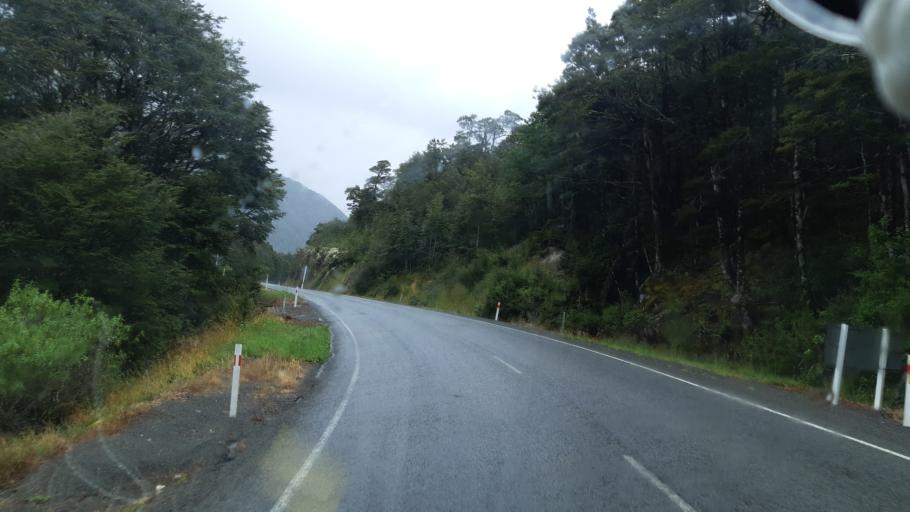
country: NZ
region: Canterbury
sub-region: Hurunui District
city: Amberley
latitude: -42.3997
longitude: 172.3991
